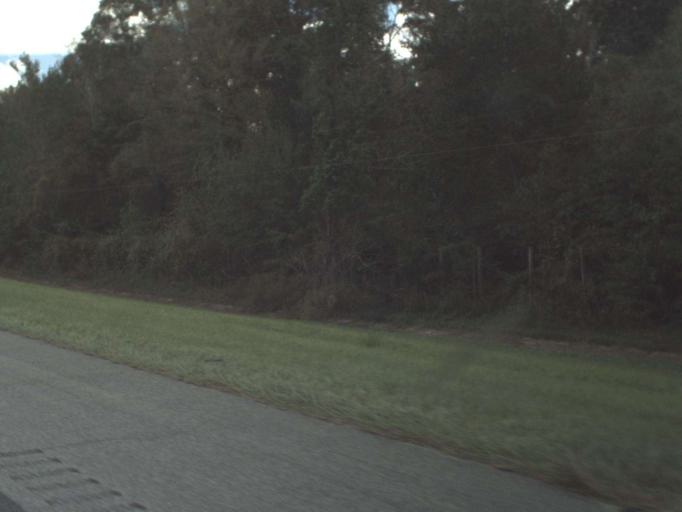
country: US
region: Florida
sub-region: Jackson County
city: Sneads
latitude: 30.6387
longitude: -84.9177
